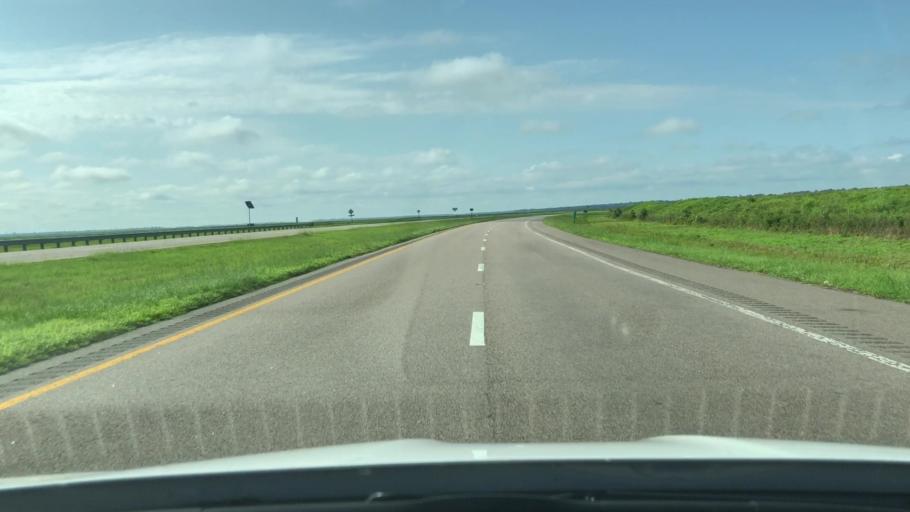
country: US
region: North Carolina
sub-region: Currituck County
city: Moyock
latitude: 36.5981
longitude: -76.3793
